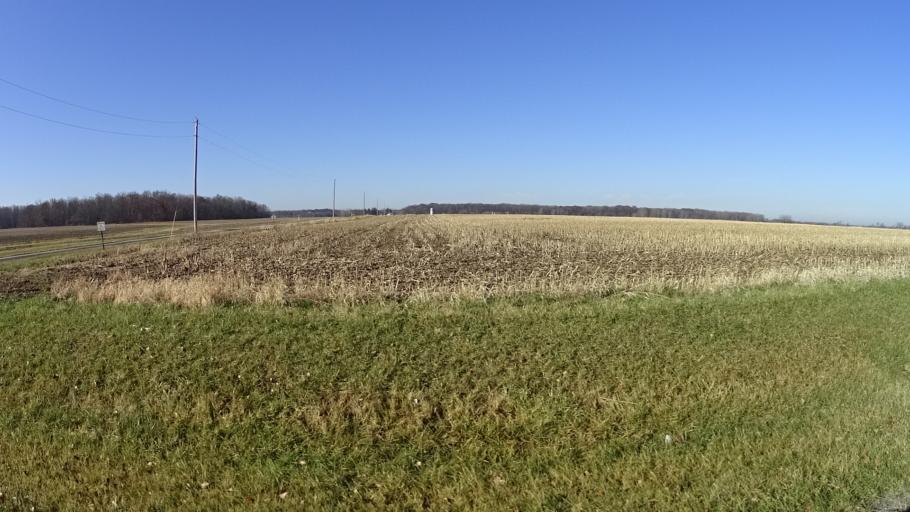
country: US
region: Ohio
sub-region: Lorain County
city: Wellington
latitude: 41.1309
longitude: -82.1801
